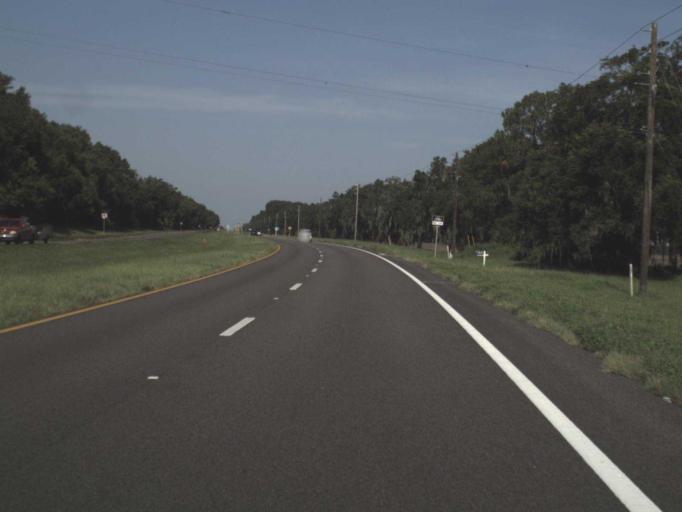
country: US
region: Florida
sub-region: Polk County
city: Willow Oak
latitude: 27.9378
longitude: -82.0915
